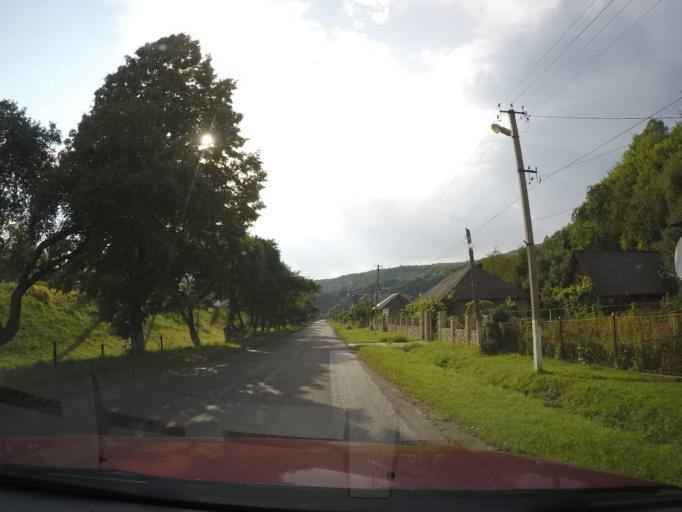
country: UA
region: Zakarpattia
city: Velykyi Bereznyi
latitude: 48.9520
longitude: 22.5344
